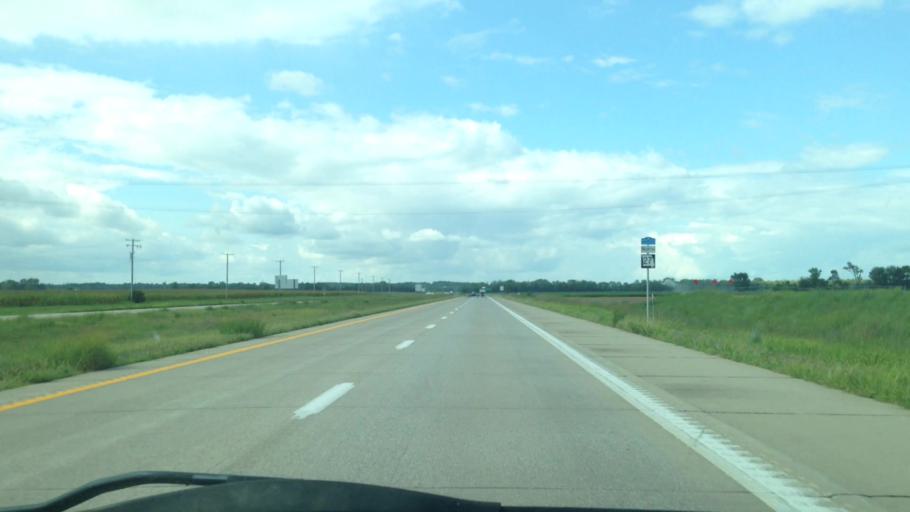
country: US
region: Illinois
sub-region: Hancock County
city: Warsaw
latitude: 40.4010
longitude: -91.5723
